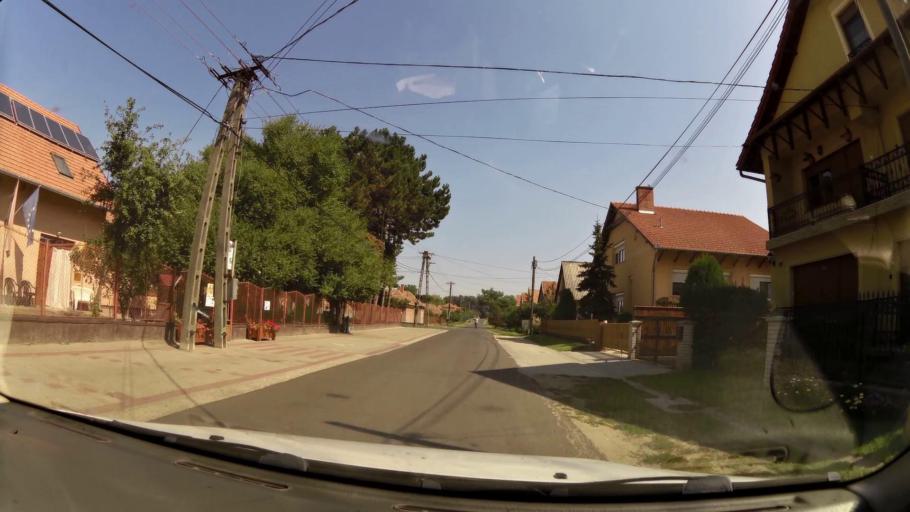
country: HU
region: Pest
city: Ujszilvas
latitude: 47.2635
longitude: 19.9139
